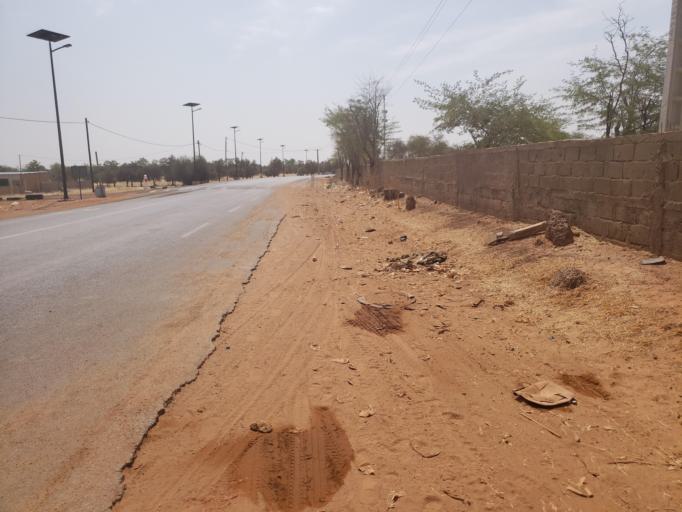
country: SN
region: Matam
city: Ranerou
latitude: 15.2971
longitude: -13.9572
